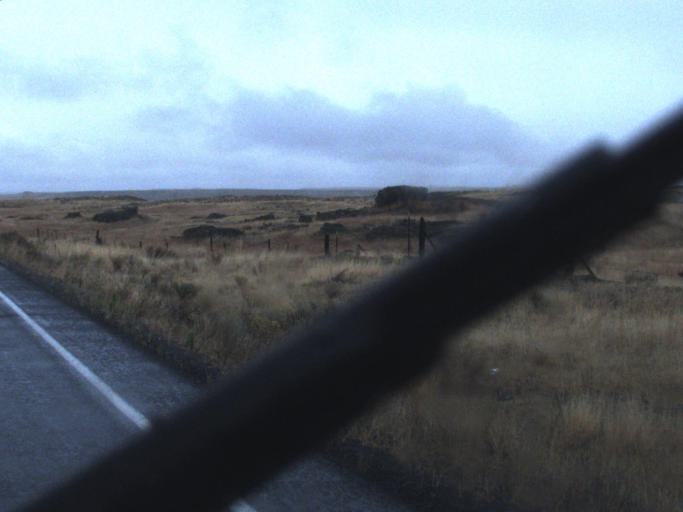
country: US
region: Washington
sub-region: Spokane County
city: Medical Lake
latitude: 47.2818
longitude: -117.9595
